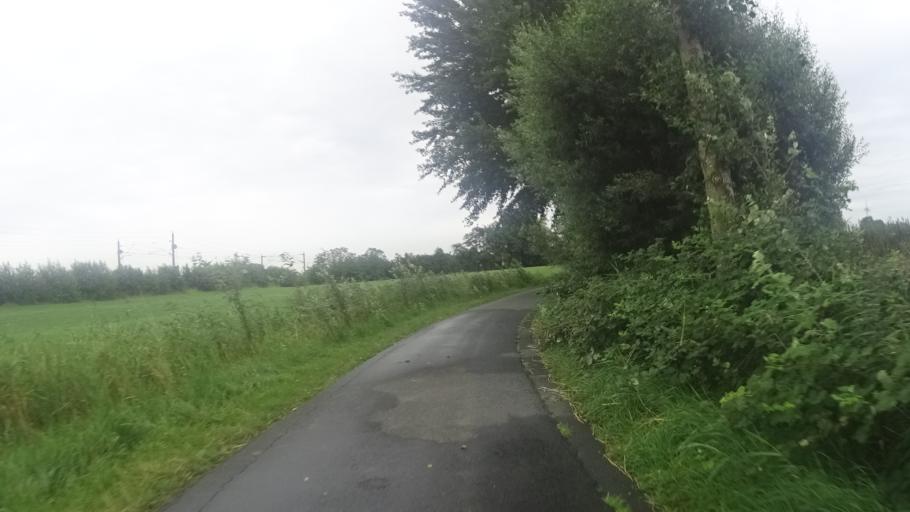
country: DE
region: Schleswig-Holstein
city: Sommerland
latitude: 53.7884
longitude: 9.5392
